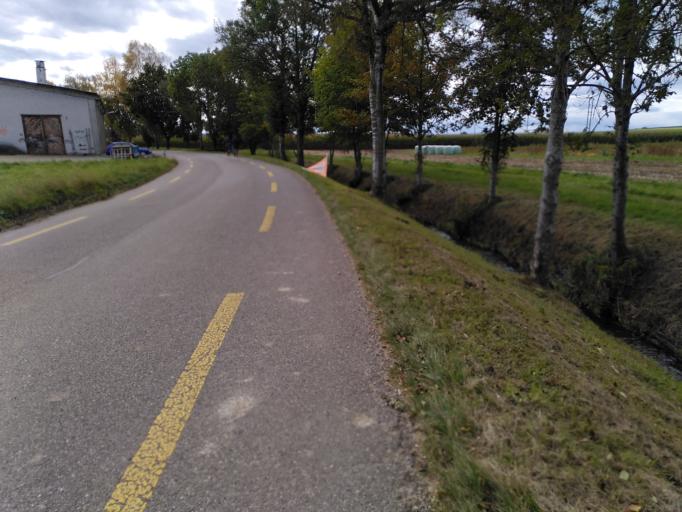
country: CH
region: Bern
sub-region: Emmental District
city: Ersigen
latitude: 47.1062
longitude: 7.6048
